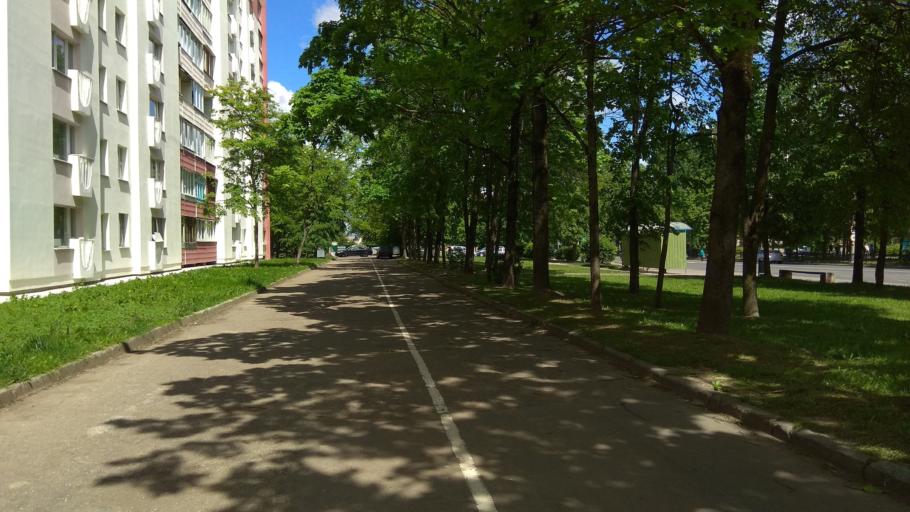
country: BY
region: Grodnenskaya
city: Hrodna
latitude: 53.7078
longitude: 23.8045
